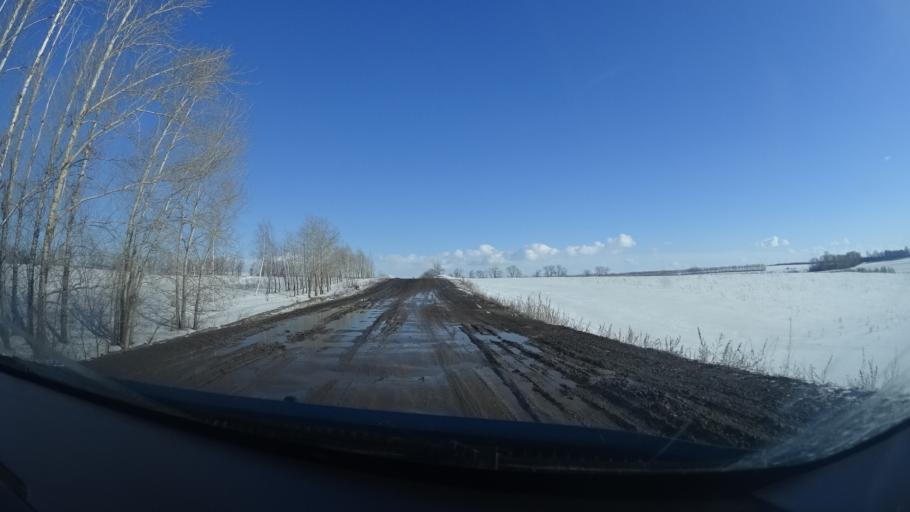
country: RU
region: Bashkortostan
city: Chishmy
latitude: 54.6003
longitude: 55.2294
